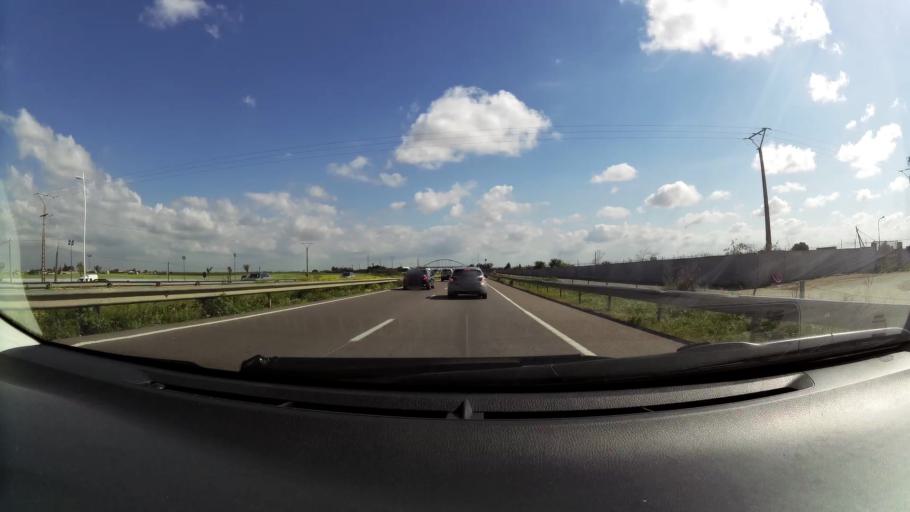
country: MA
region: Chaouia-Ouardigha
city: Nouaseur
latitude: 33.3745
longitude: -7.6215
